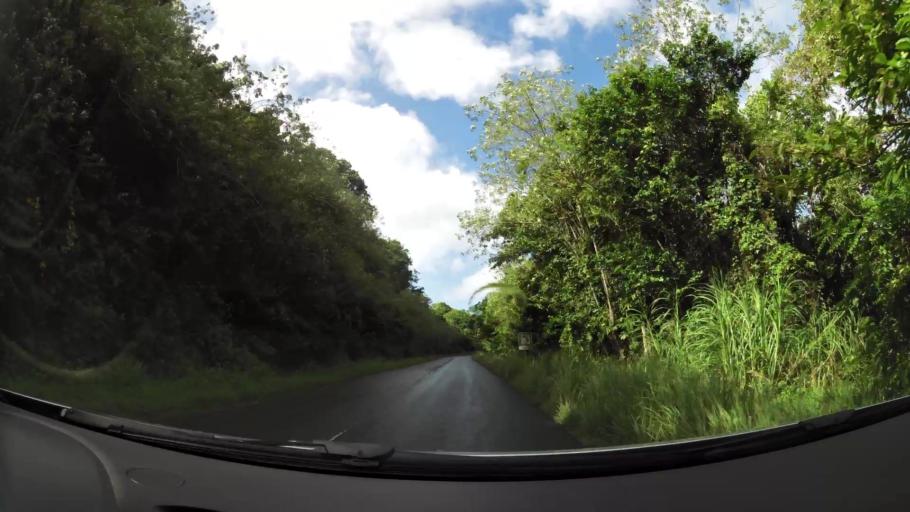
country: MQ
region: Martinique
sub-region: Martinique
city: Les Trois-Ilets
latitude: 14.5350
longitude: -61.0514
